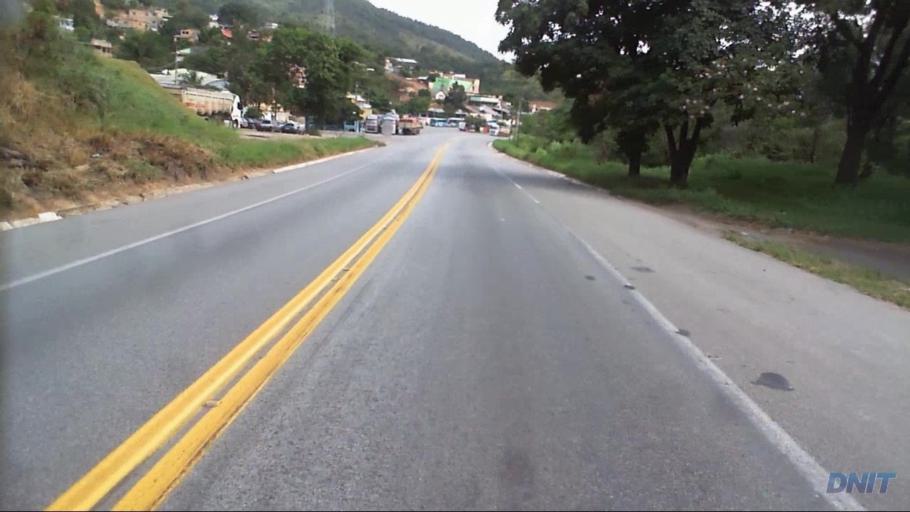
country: BR
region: Minas Gerais
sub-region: Santa Luzia
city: Santa Luzia
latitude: -19.8307
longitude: -43.8446
